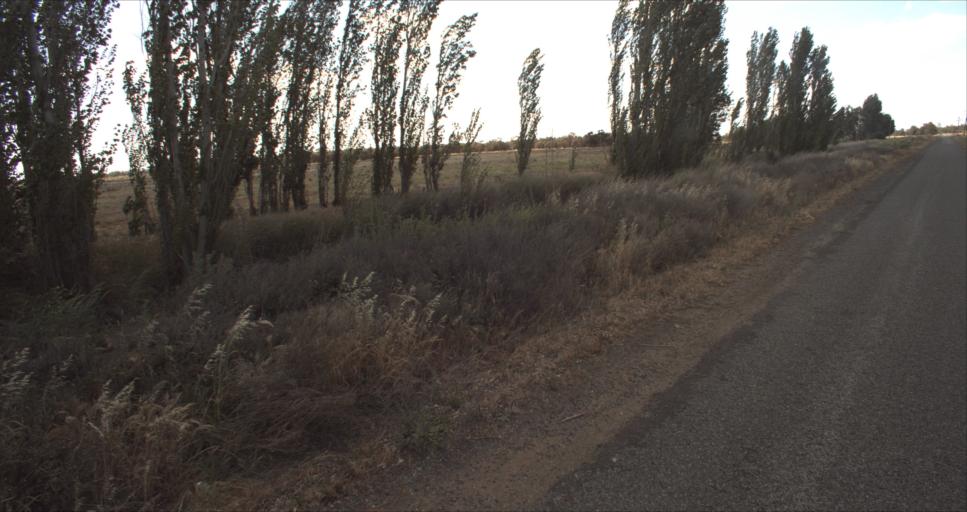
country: AU
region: New South Wales
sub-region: Leeton
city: Leeton
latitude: -34.5278
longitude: 146.2200
